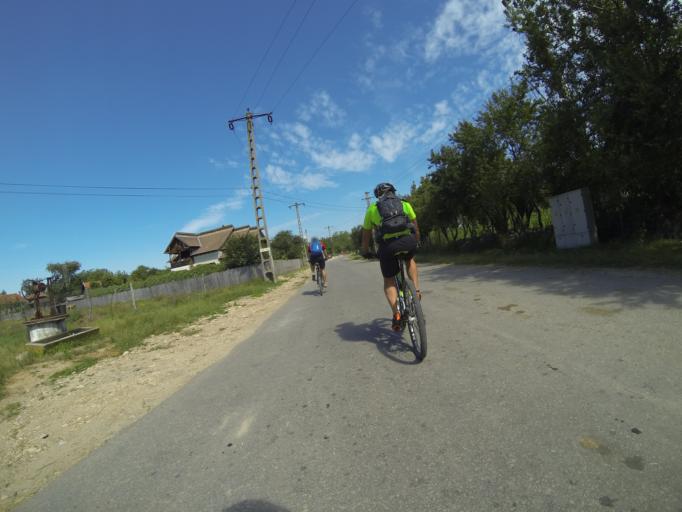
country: RO
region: Gorj
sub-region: Comuna Polovragi
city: Polovragi
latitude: 45.1653
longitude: 23.8111
